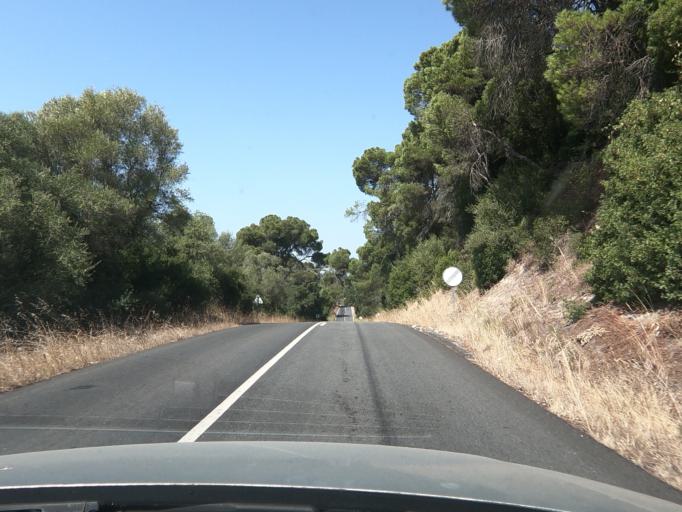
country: PT
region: Setubal
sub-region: Alcacer do Sal
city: Alcacer do Sal
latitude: 38.3583
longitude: -8.4754
